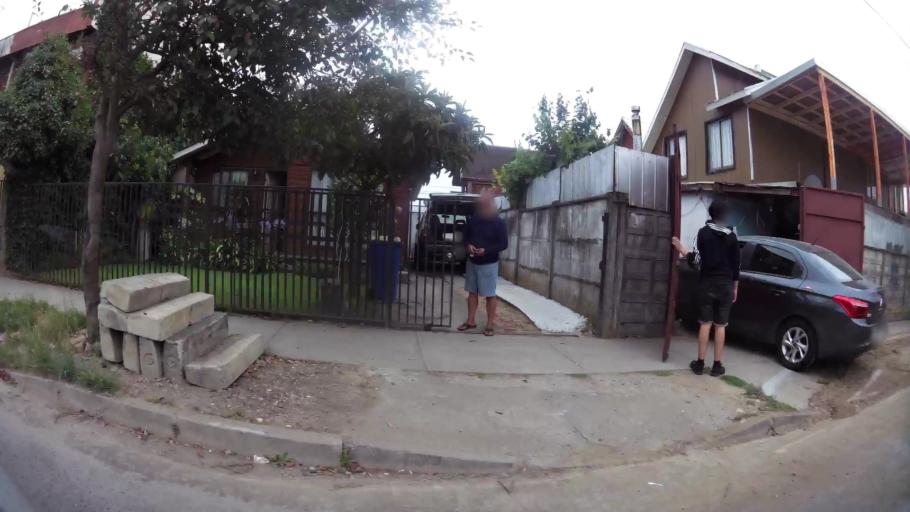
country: CL
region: Biobio
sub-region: Provincia de Concepcion
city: Concepcion
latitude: -36.8328
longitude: -73.0101
